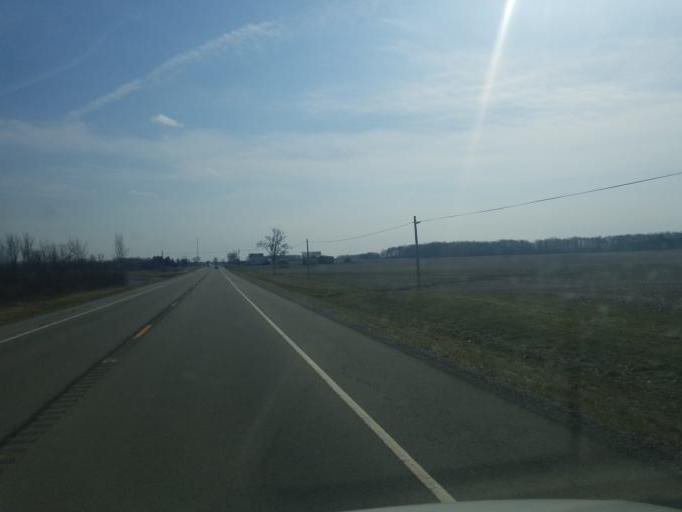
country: US
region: Ohio
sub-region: Logan County
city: Northwood
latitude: 40.5279
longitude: -83.6816
